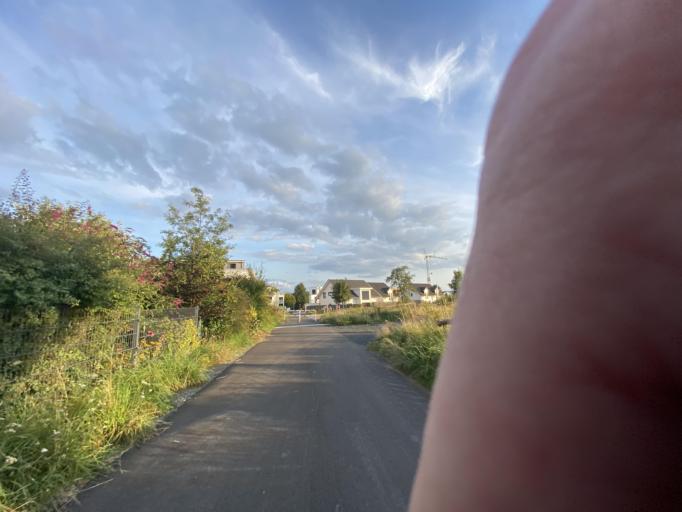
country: DE
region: Hesse
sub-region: Regierungsbezirk Darmstadt
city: Dietzenbach
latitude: 49.9824
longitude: 8.7945
